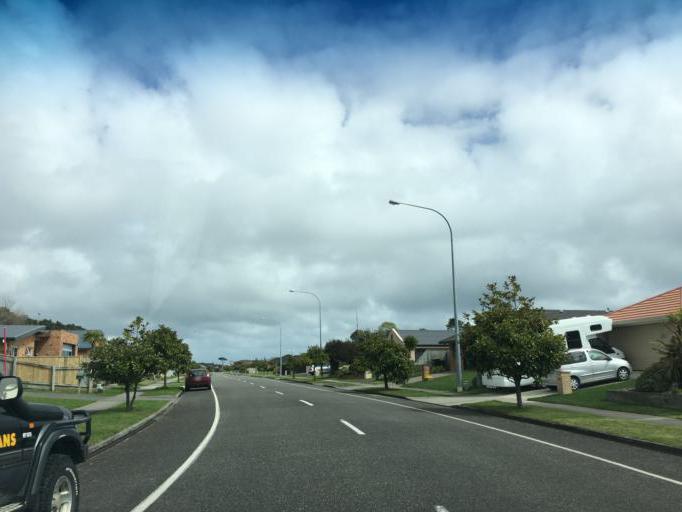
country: NZ
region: Wellington
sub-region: Kapiti Coast District
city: Paraparaumu
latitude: -40.8746
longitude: 175.0198
